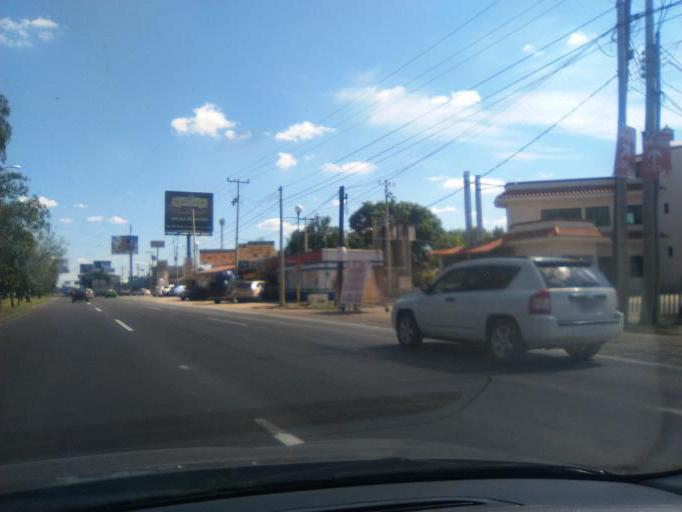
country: MX
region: Guanajuato
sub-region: Leon
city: Ladrilleras del Refugio
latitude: 21.0700
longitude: -101.5955
